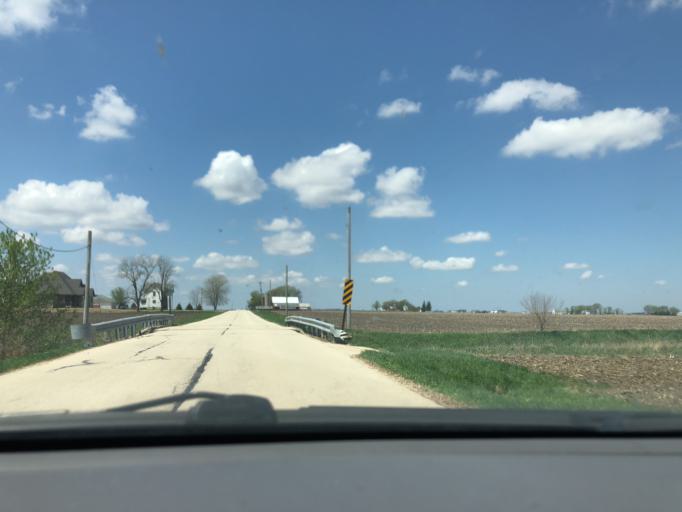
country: US
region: Illinois
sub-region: Kane County
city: Hampshire
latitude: 42.1101
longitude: -88.5899
